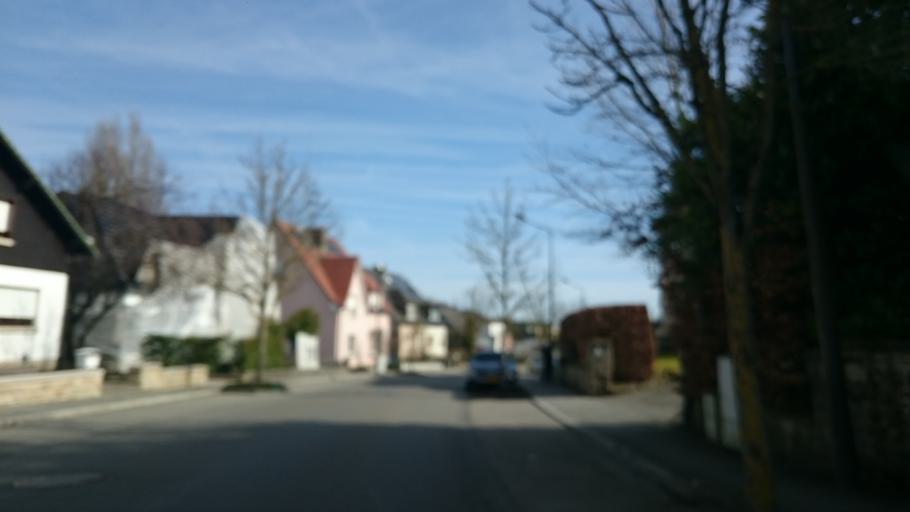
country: LU
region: Luxembourg
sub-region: Canton de Luxembourg
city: Luxembourg
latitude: 49.5886
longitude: 6.1120
